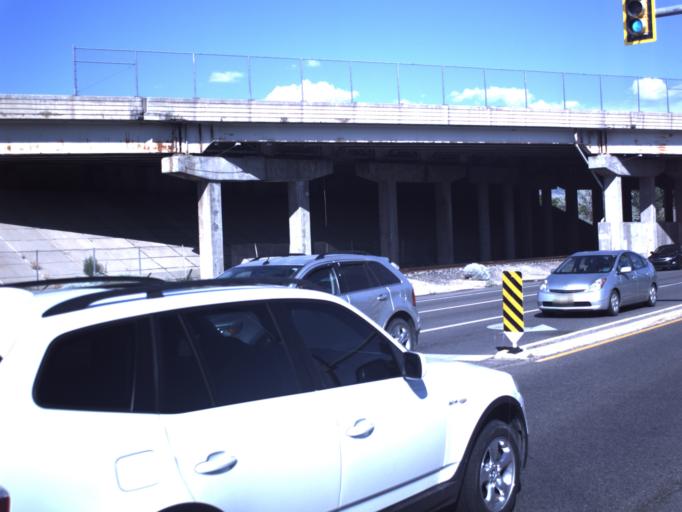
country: US
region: Utah
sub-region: Utah County
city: Lehi
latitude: 40.3927
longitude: -111.8370
